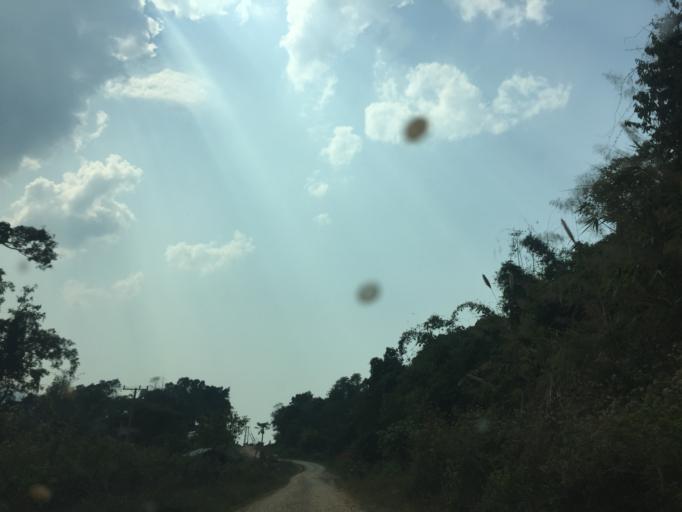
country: TH
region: Nan
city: Song Khwae
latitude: 19.7452
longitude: 100.7032
